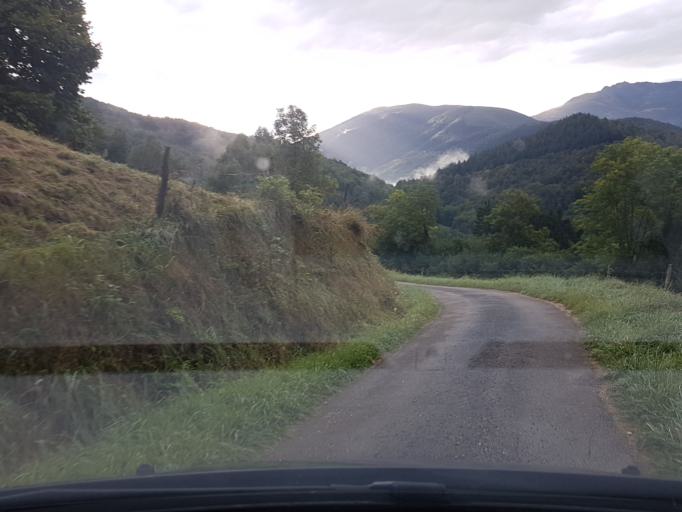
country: FR
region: Midi-Pyrenees
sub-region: Departement de l'Ariege
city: Foix
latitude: 42.9111
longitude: 1.3773
